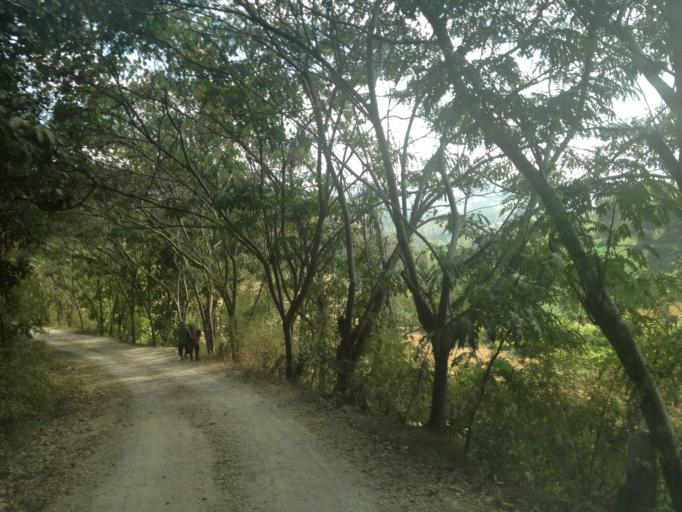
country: TH
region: Mae Hong Son
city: Ban Huai I Huak
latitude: 18.0924
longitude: 98.1891
